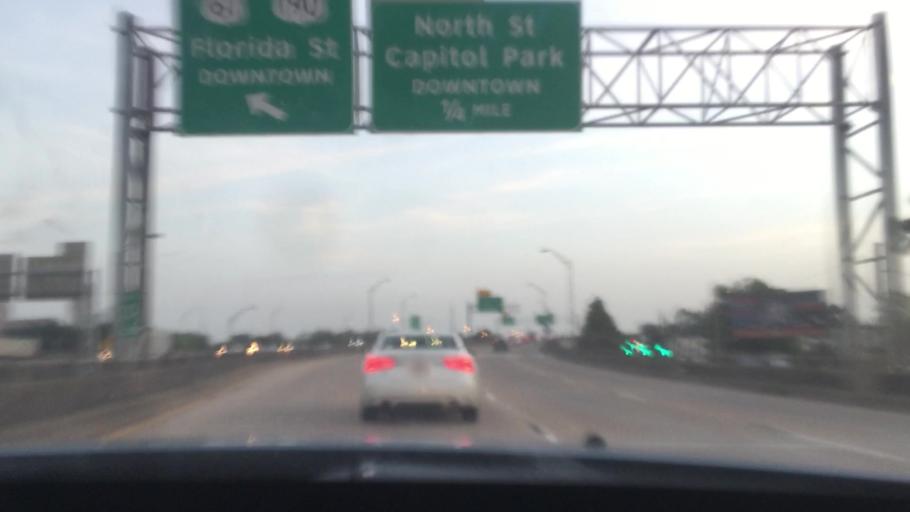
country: US
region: Louisiana
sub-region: East Baton Rouge Parish
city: Baton Rouge
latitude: 30.4472
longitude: -91.1798
